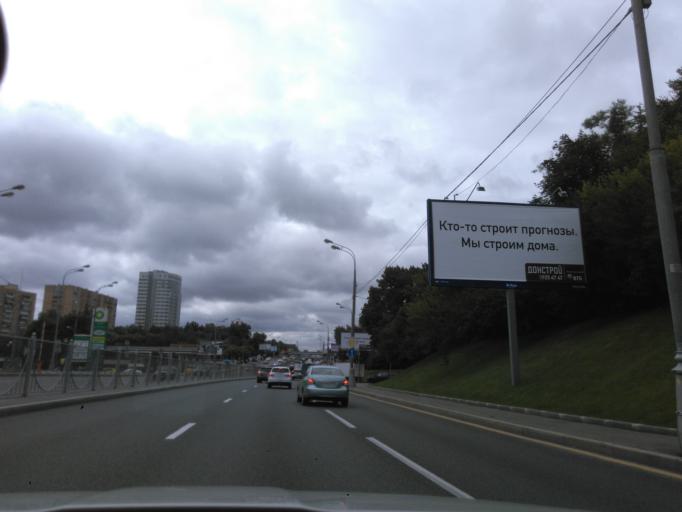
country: RU
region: Moscow
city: Davydkovo
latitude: 55.7325
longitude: 37.4451
